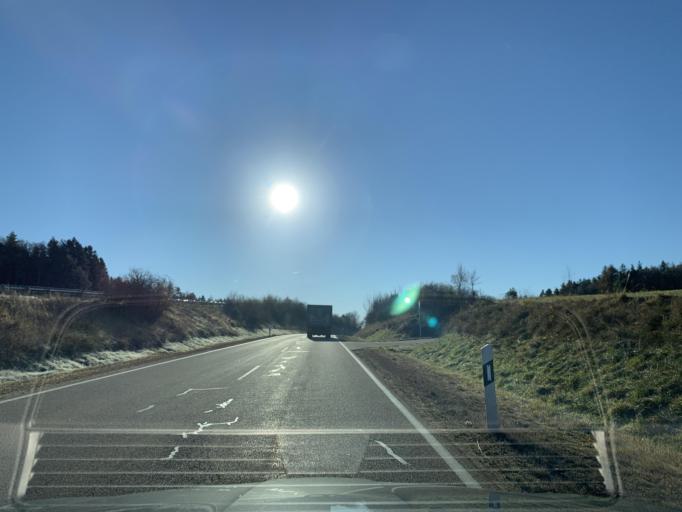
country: DE
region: Bavaria
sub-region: Upper Palatinate
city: Oberviechtach
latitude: 49.4389
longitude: 12.4175
